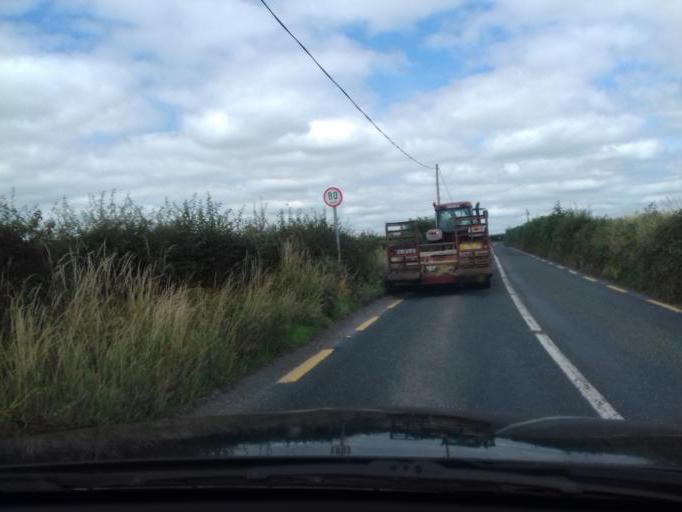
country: IE
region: Leinster
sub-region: County Carlow
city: Tullow
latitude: 52.8256
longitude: -6.7230
